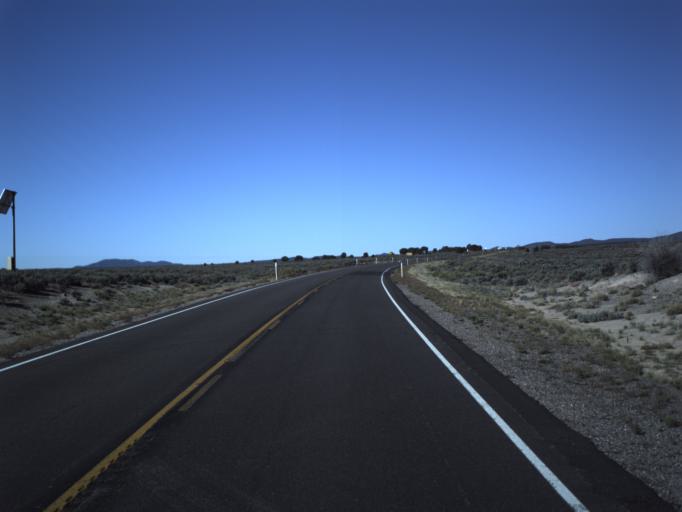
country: US
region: Utah
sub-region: Washington County
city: Enterprise
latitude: 37.7241
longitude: -114.0418
